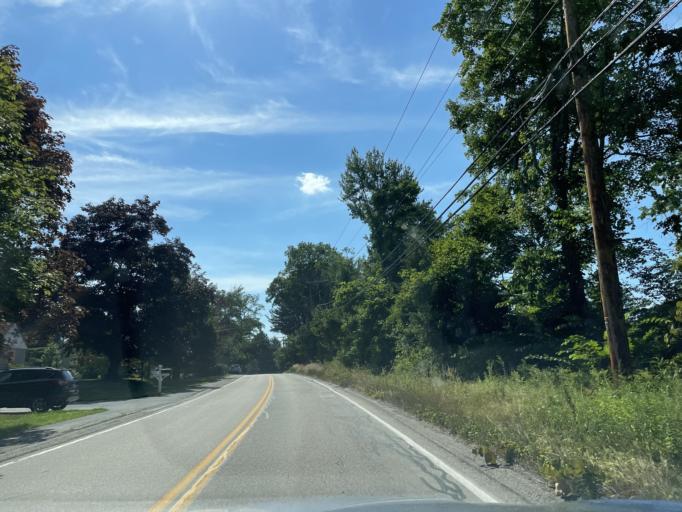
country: US
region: Massachusetts
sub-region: Worcester County
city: Mendon
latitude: 42.1162
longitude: -71.5670
